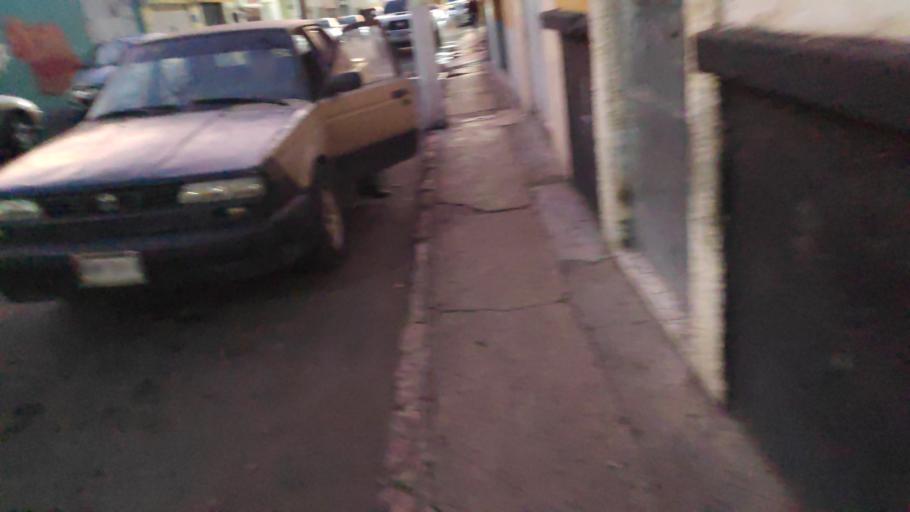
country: MX
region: Queretaro
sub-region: Queretaro
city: Santiago de Queretaro
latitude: 20.5890
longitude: -100.3801
